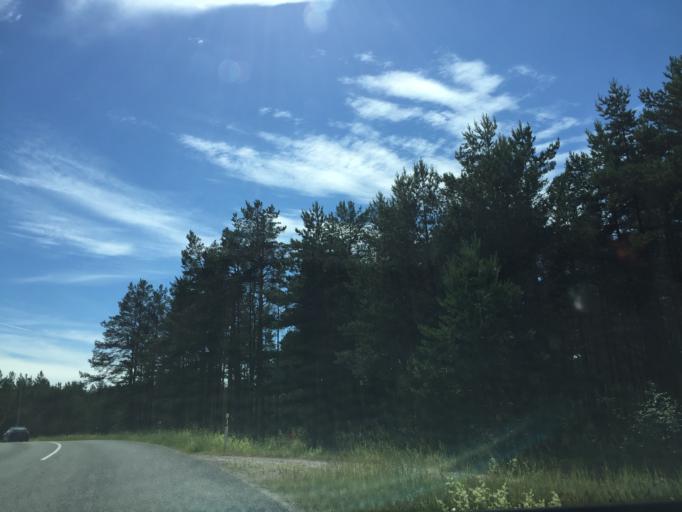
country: LV
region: Dundaga
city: Dundaga
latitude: 57.6488
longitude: 22.5721
